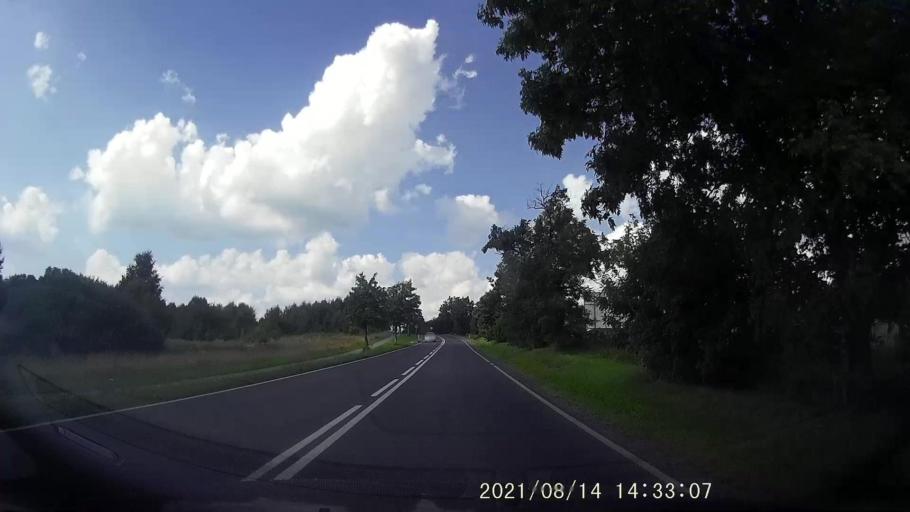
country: PL
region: Lower Silesian Voivodeship
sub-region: Powiat klodzki
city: Nowa Ruda
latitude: 50.5555
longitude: 16.5460
